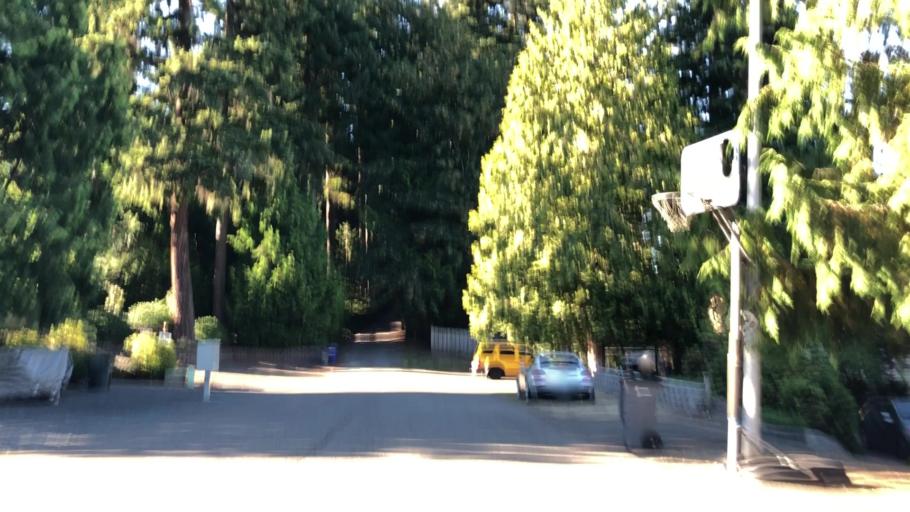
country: US
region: Washington
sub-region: King County
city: Bothell
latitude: 47.7956
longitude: -122.2276
